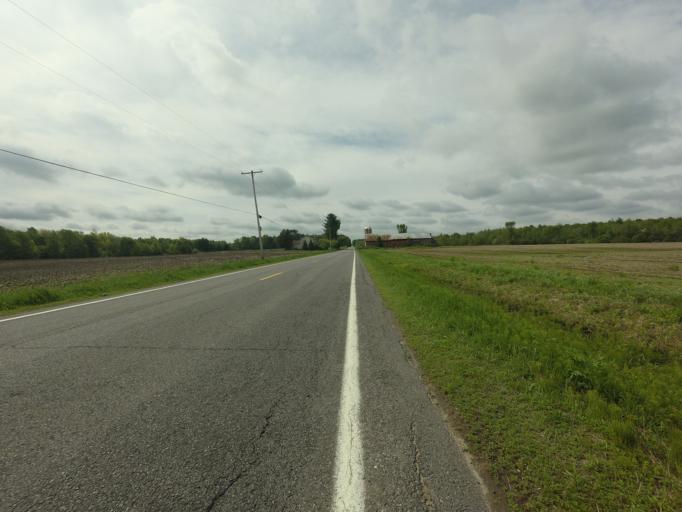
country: CA
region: Ontario
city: Cornwall
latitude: 44.7503
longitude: -74.6682
